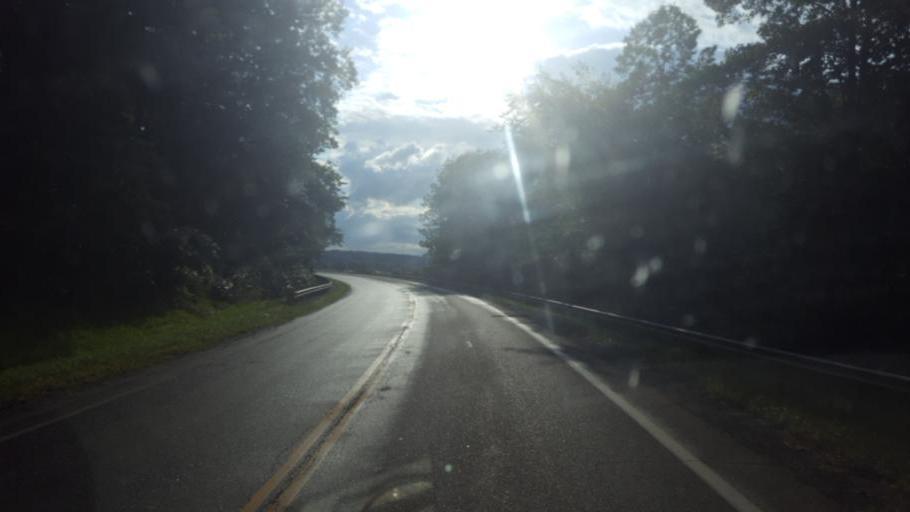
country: US
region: Ohio
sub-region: Holmes County
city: Millersburg
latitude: 40.5050
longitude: -81.9680
